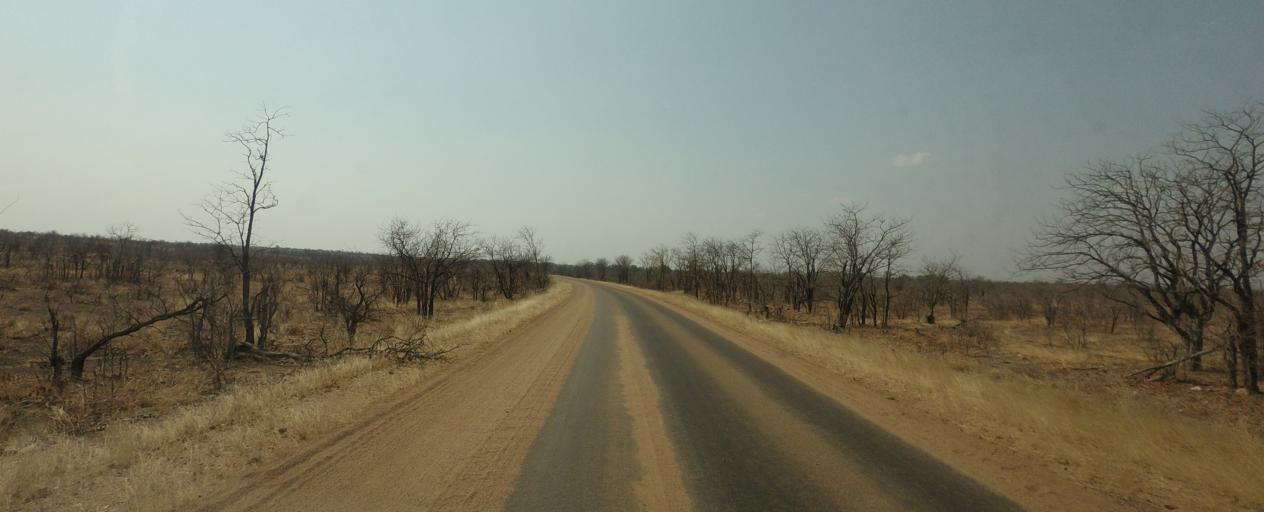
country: ZA
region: Limpopo
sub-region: Mopani District Municipality
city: Giyani
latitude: -23.2143
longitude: 31.3163
